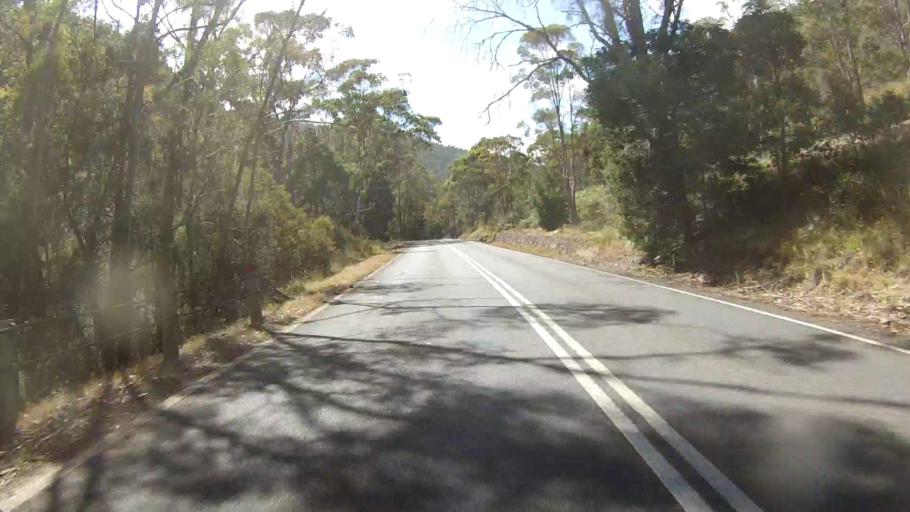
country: AU
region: Tasmania
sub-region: Derwent Valley
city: New Norfolk
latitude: -42.6797
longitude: 146.7527
